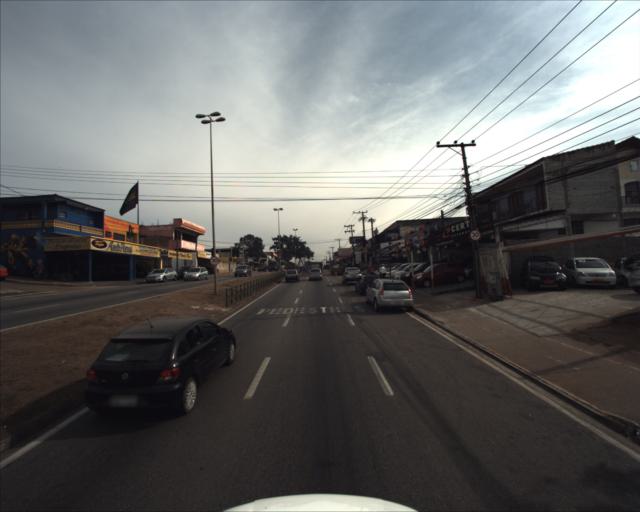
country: BR
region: Sao Paulo
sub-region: Sorocaba
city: Sorocaba
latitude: -23.4777
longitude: -47.4844
